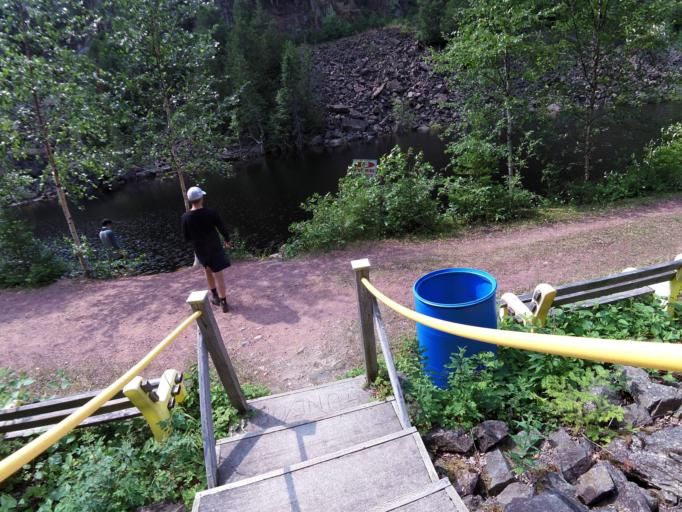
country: CA
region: Ontario
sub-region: Thunder Bay District
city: Thunder Bay
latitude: 48.8005
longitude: -88.6175
